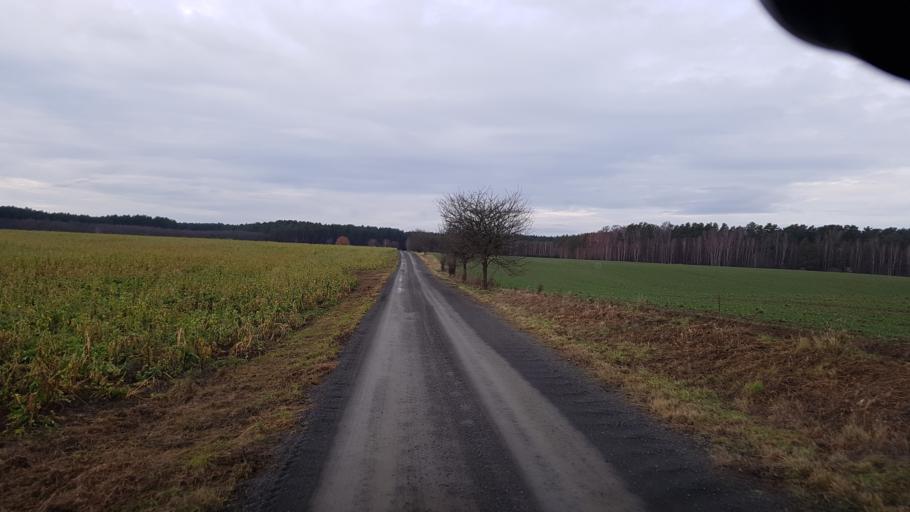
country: DE
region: Brandenburg
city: Hohenbucko
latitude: 51.7705
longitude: 13.4525
